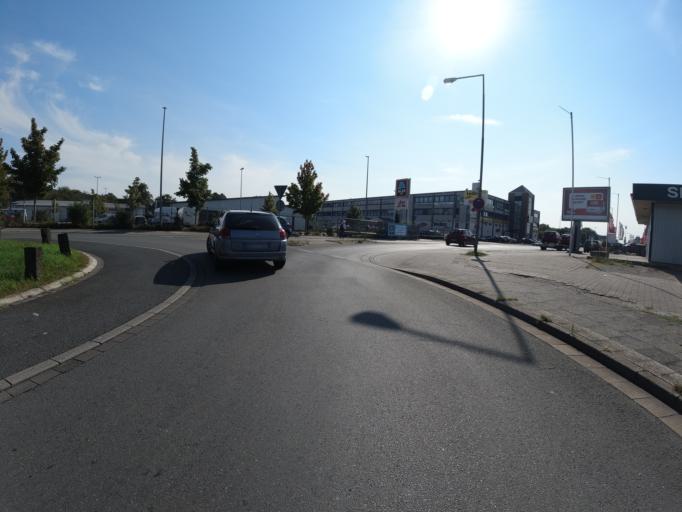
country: DE
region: North Rhine-Westphalia
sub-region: Regierungsbezirk Dusseldorf
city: Moers
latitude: 51.4564
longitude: 6.6676
